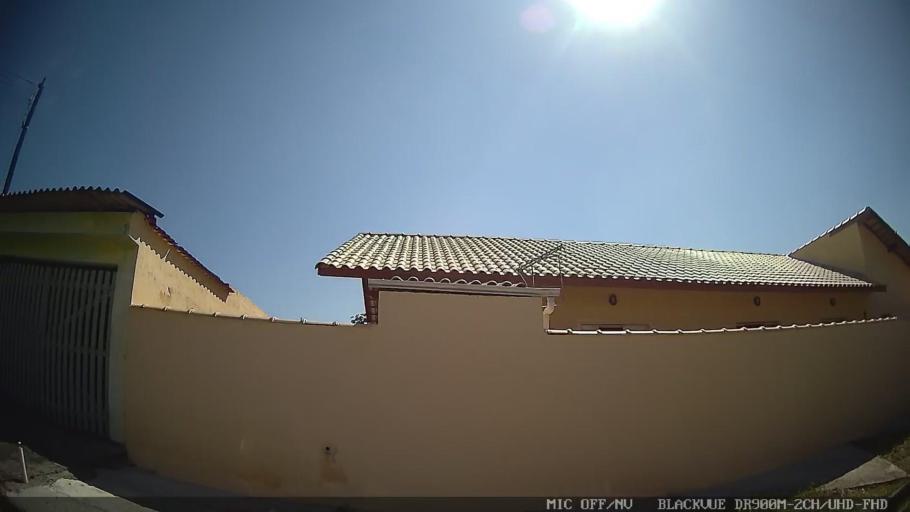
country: BR
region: Sao Paulo
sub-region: Itanhaem
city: Itanhaem
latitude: -24.1496
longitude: -46.7338
